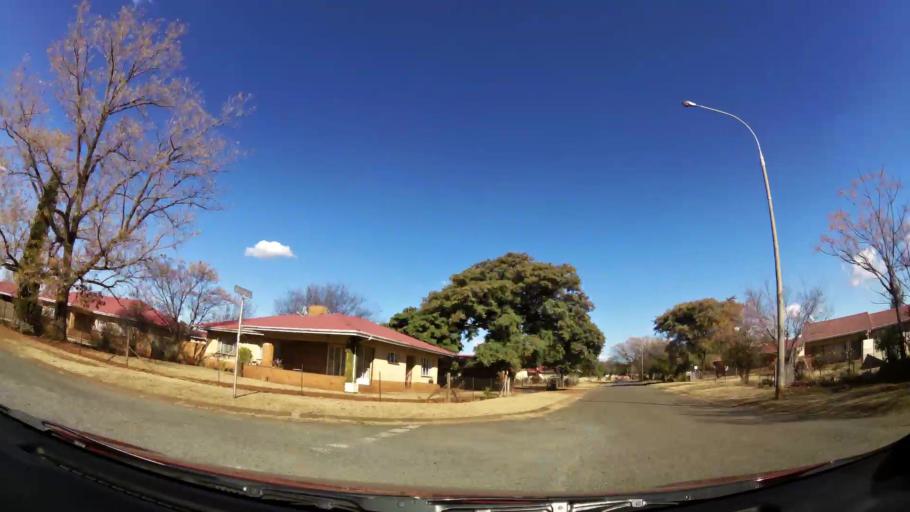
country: ZA
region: Gauteng
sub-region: West Rand District Municipality
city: Carletonville
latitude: -26.3649
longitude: 27.3622
